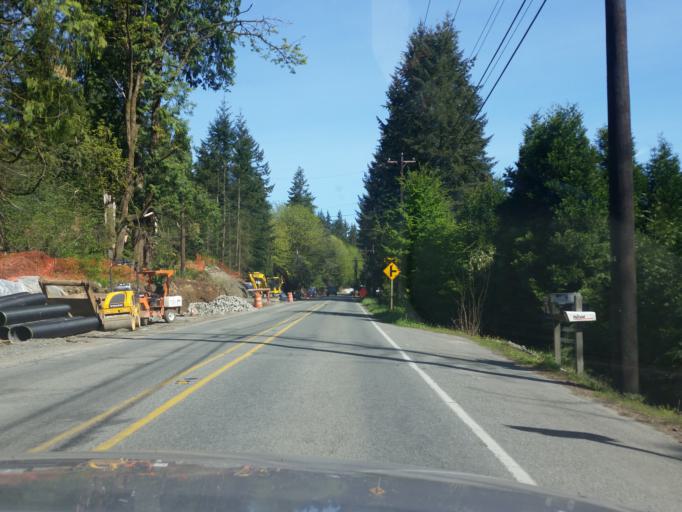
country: US
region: Washington
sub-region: Snohomish County
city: Clearview
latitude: 47.8287
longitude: -122.1098
